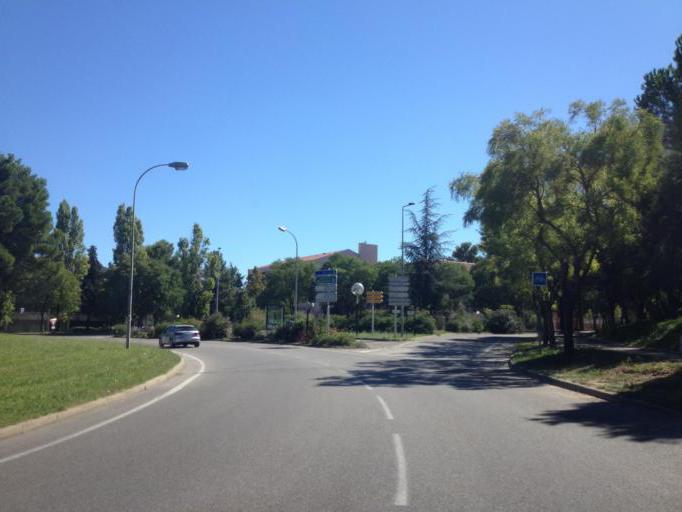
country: FR
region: Provence-Alpes-Cote d'Azur
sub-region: Departement des Bouches-du-Rhone
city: Aix-en-Provence
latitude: 43.5302
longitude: 5.4156
